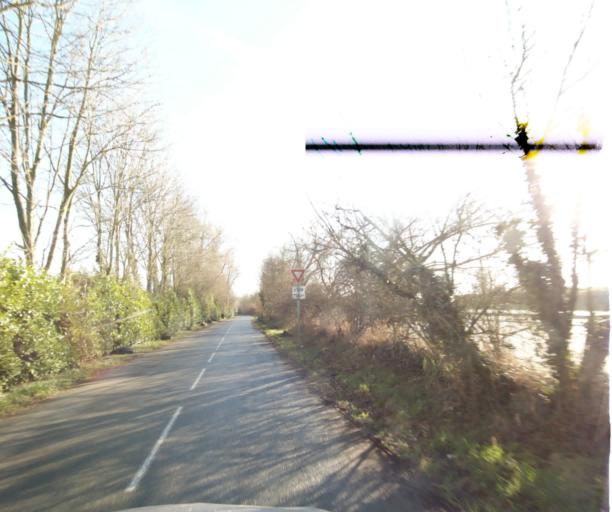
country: FR
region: Nord-Pas-de-Calais
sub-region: Departement du Nord
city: Curgies
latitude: 50.3252
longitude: 3.5976
